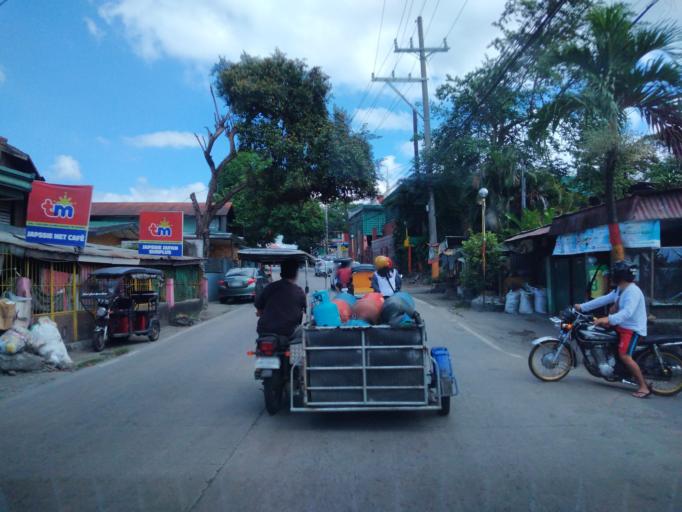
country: PH
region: Central Luzon
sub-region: Province of Bulacan
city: Guyong
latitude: 14.8343
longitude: 120.9756
